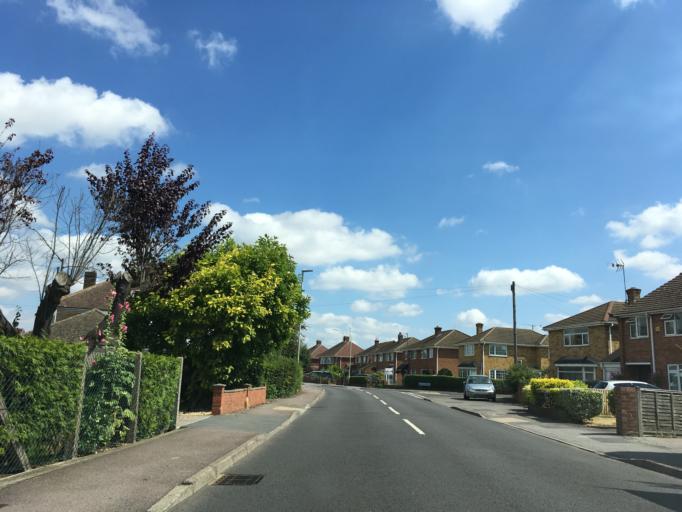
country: GB
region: England
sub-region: Gloucestershire
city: Barnwood
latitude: 51.8805
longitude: -2.2147
